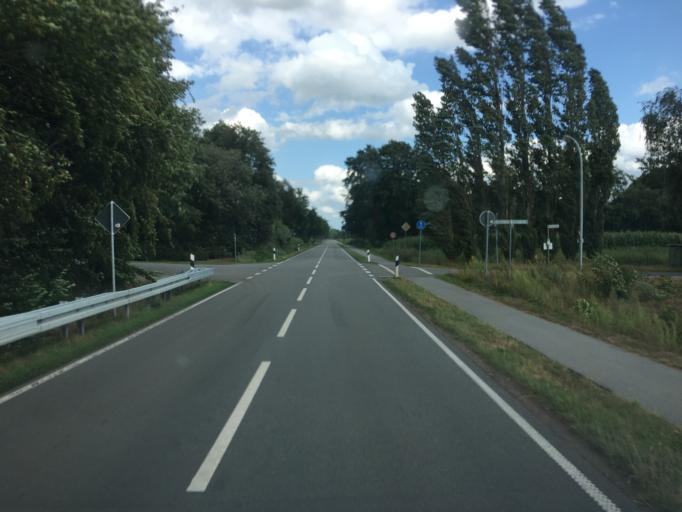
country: DE
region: Lower Saxony
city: Barssel
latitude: 53.0808
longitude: 7.7685
